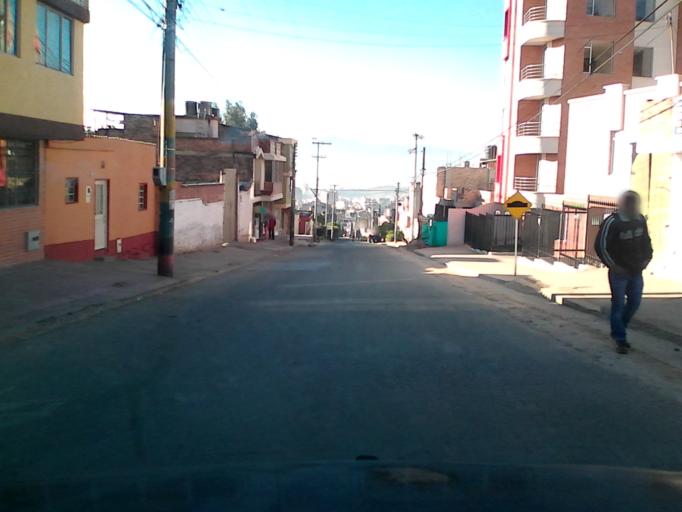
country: CO
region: Boyaca
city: Duitama
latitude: 5.8415
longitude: -73.0368
